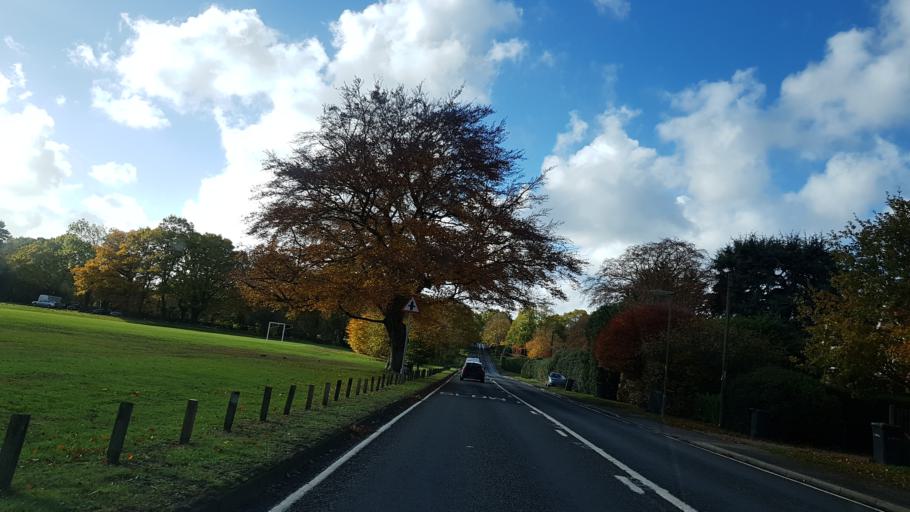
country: GB
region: England
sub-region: Surrey
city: Milford
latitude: 51.1667
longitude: -0.6514
